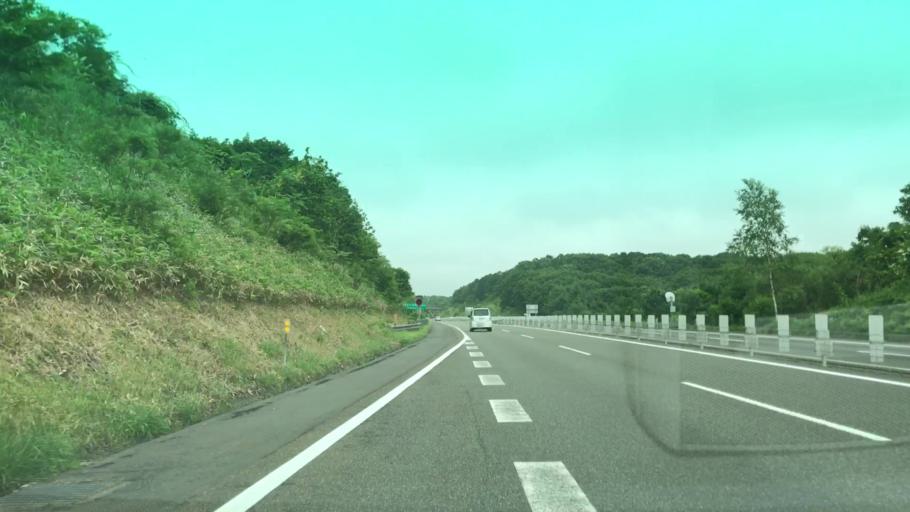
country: JP
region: Hokkaido
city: Tomakomai
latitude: 42.6174
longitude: 141.4730
